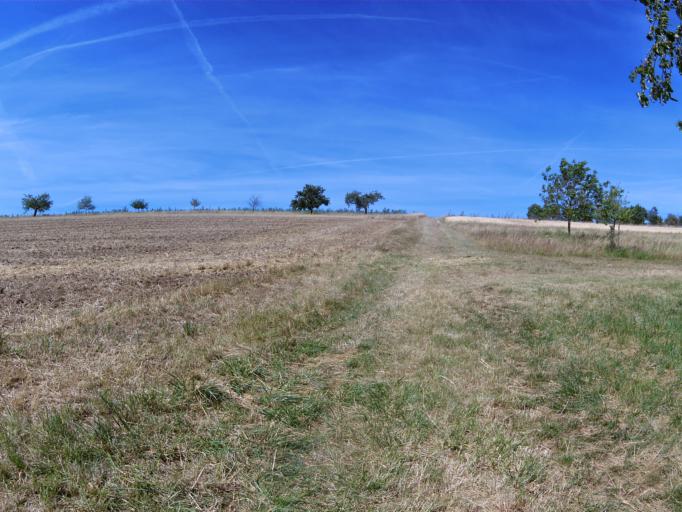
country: DE
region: Bavaria
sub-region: Regierungsbezirk Unterfranken
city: Hettstadt
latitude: 49.8069
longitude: 9.8149
